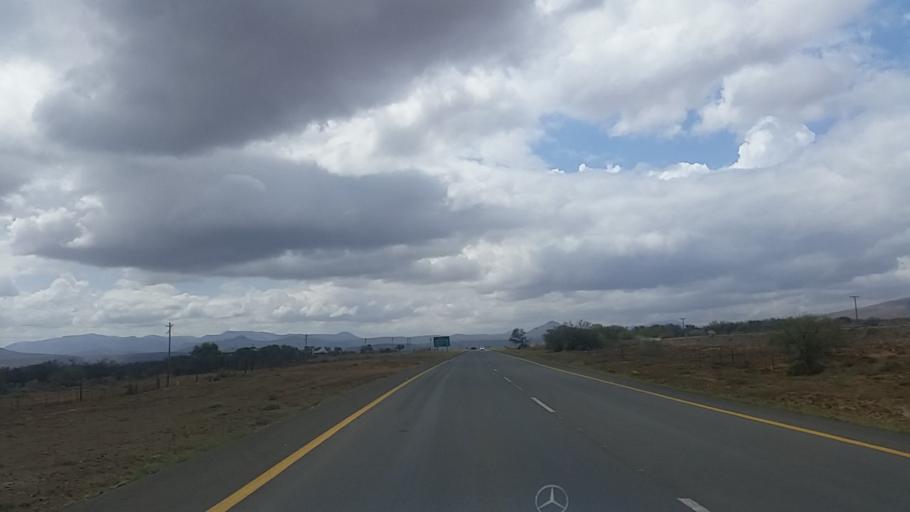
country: ZA
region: Eastern Cape
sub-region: Cacadu District Municipality
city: Graaff-Reinet
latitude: -32.2247
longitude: 24.5393
